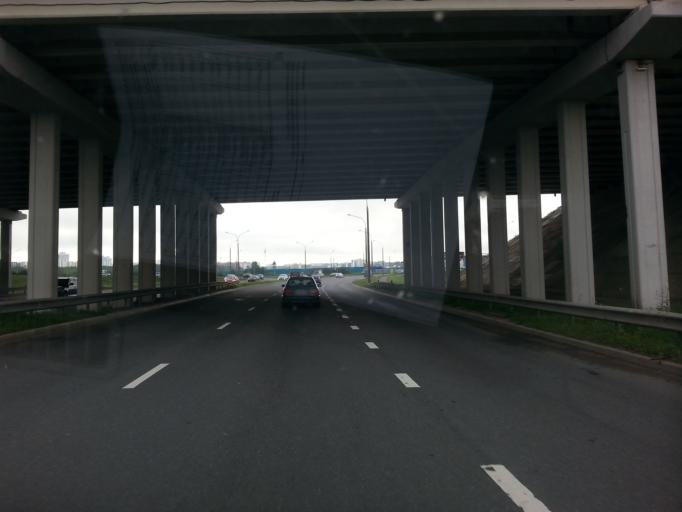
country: BY
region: Minsk
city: Zhdanovichy
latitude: 53.9441
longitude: 27.4359
